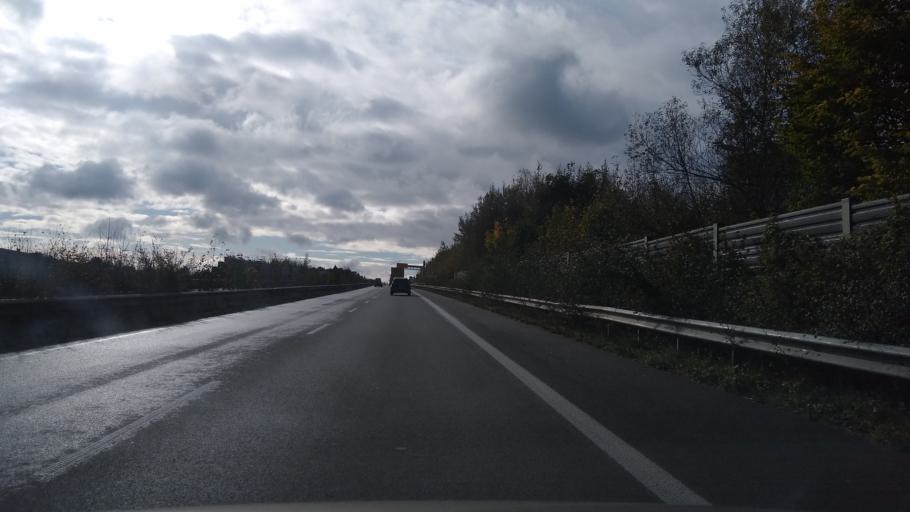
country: DE
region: Lower Saxony
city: Cloppenburg
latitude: 52.8461
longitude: 8.0248
